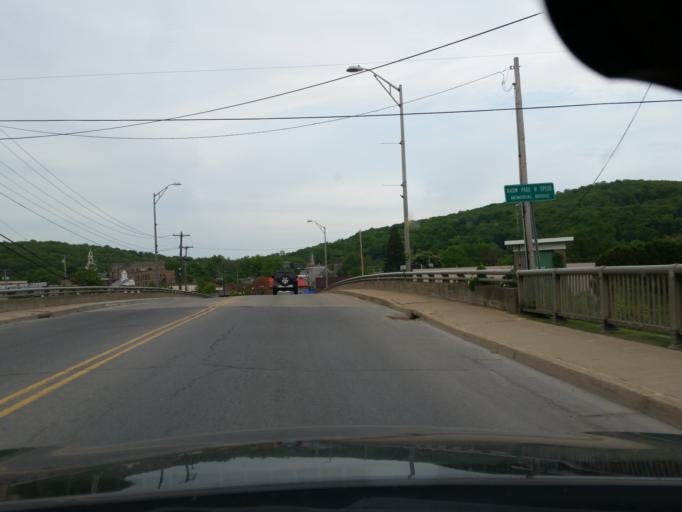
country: US
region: Pennsylvania
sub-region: Elk County
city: Ridgway
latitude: 41.4208
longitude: -78.7362
